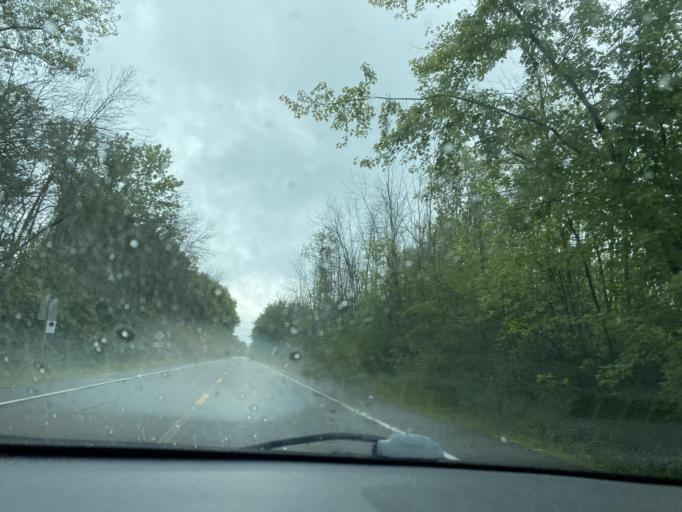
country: CA
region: Quebec
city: Baie-D'Urfe
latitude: 45.4491
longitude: -73.9343
